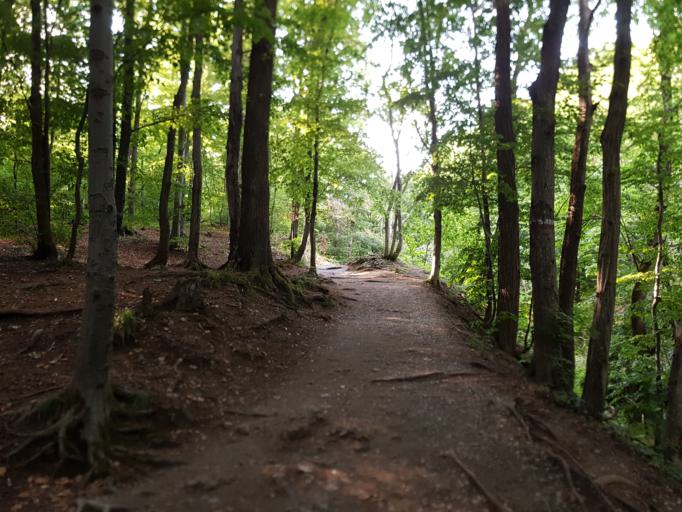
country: HR
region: Grad Zagreb
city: Zagreb
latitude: 45.8683
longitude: 15.9458
